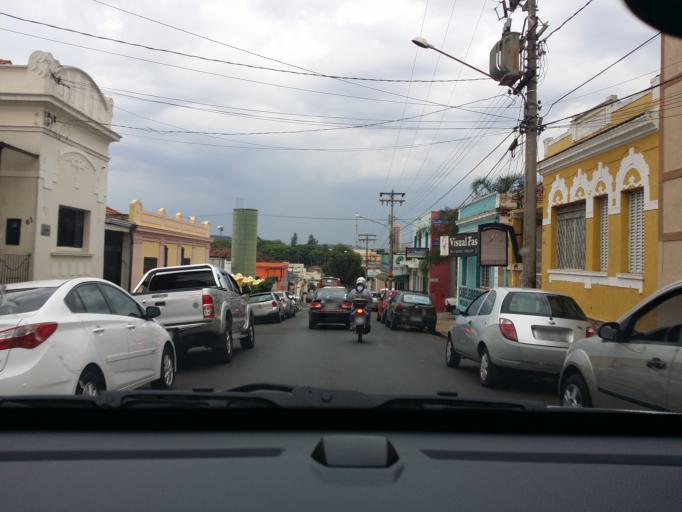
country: BR
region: Sao Paulo
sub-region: Sao Carlos
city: Sao Carlos
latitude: -22.0235
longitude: -47.8944
